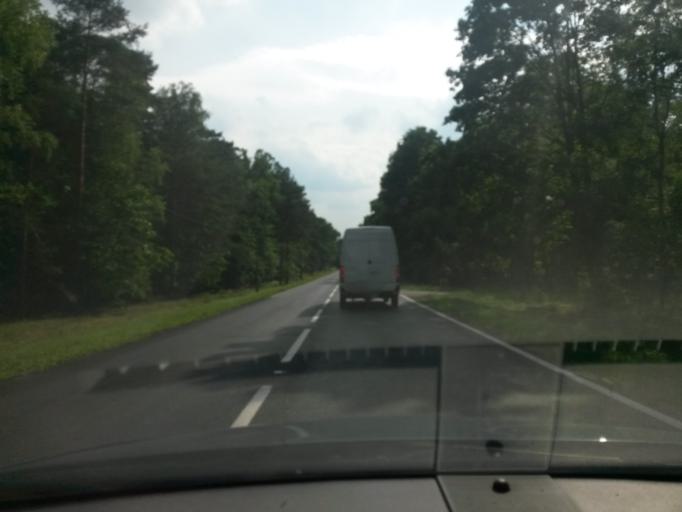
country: PL
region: Greater Poland Voivodeship
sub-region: Powiat poznanski
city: Kornik
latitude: 52.1737
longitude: 17.0446
